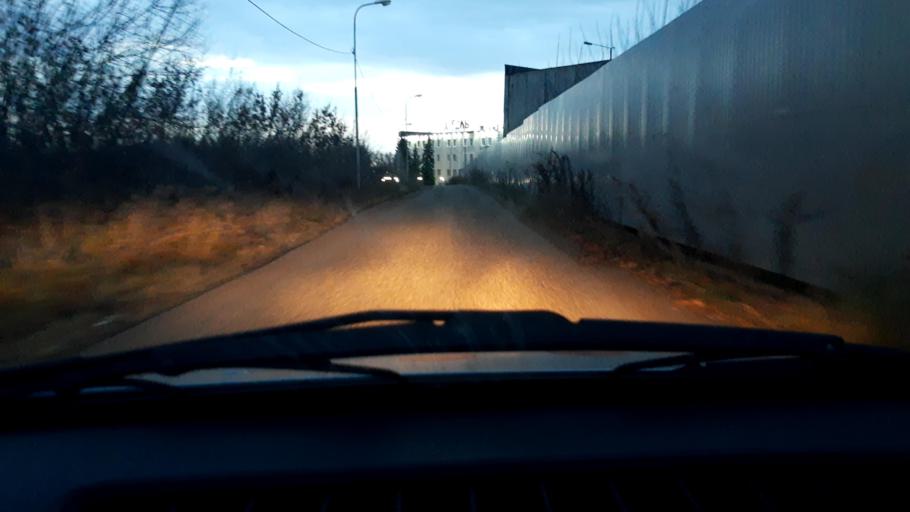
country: RU
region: Bashkortostan
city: Avdon
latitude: 54.6750
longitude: 55.8056
